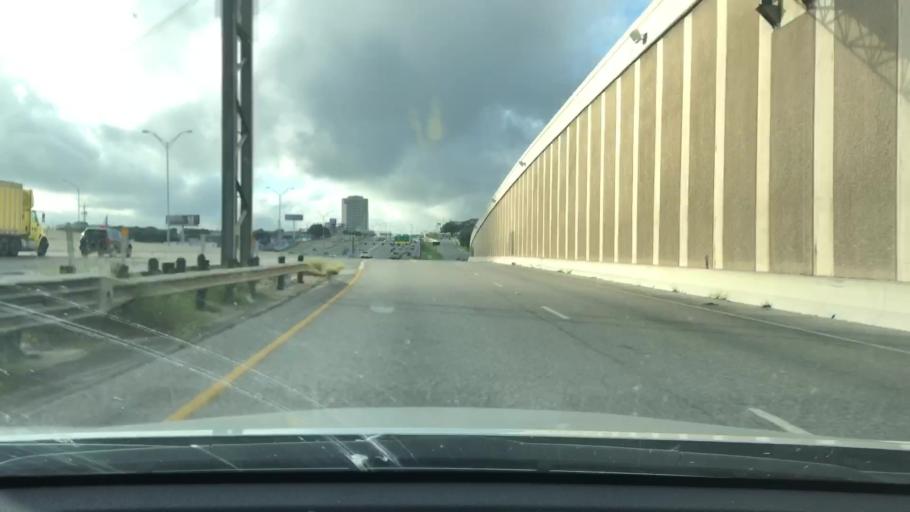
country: US
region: Texas
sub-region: Bexar County
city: Balcones Heights
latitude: 29.5215
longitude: -98.5557
